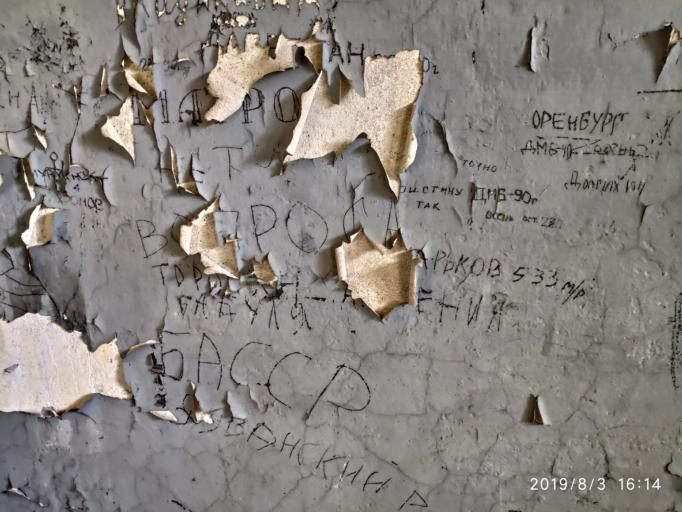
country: PL
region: Lubusz
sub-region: Powiat zaganski
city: Szprotawa
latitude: 51.4465
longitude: 15.5670
